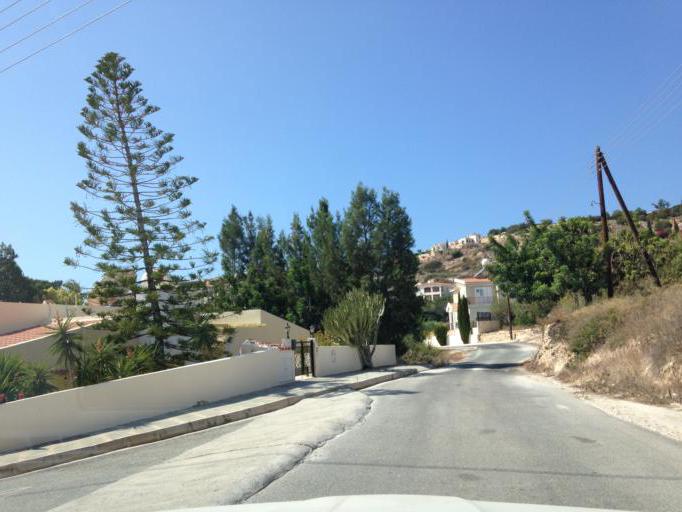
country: CY
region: Pafos
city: Pegeia
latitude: 34.8829
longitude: 32.3719
